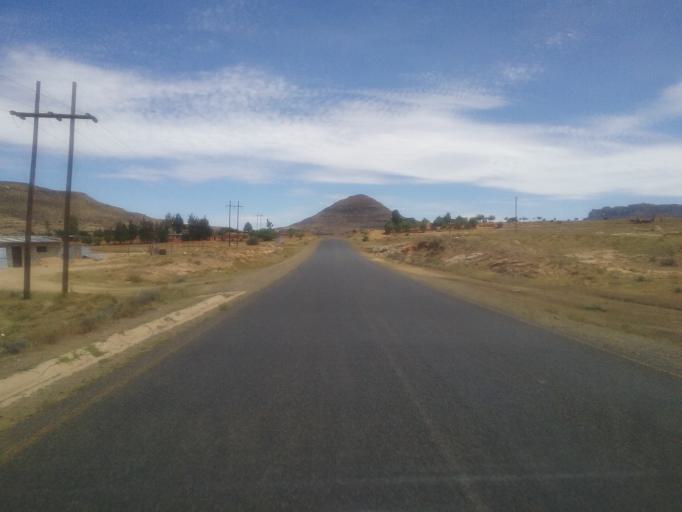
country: LS
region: Mafeteng
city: Mafeteng
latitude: -29.9683
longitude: 27.3058
